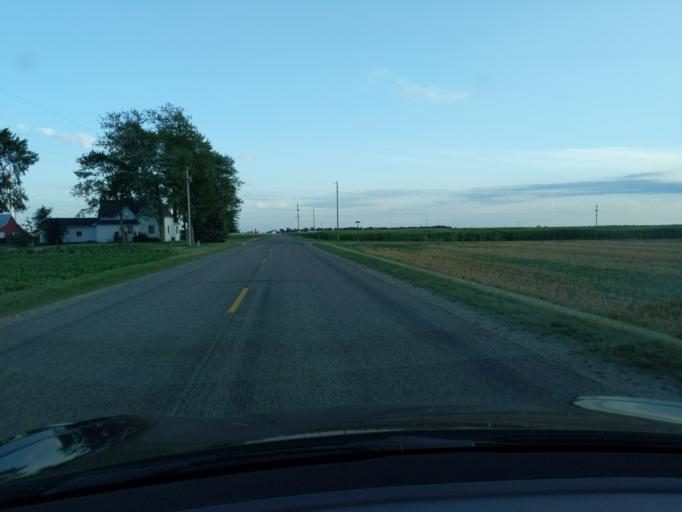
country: US
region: Michigan
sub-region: Gratiot County
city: Saint Louis
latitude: 43.3943
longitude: -84.5481
